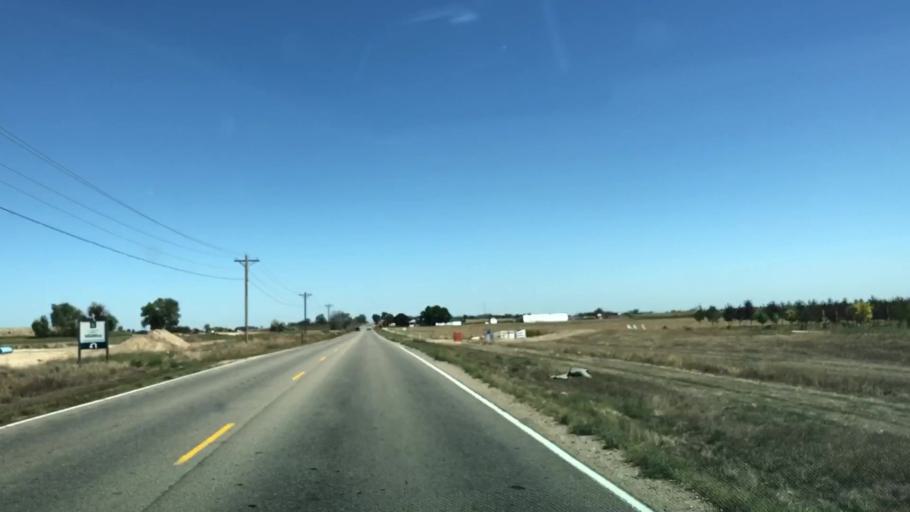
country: US
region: Colorado
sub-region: Weld County
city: Windsor
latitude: 40.5228
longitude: -104.9374
